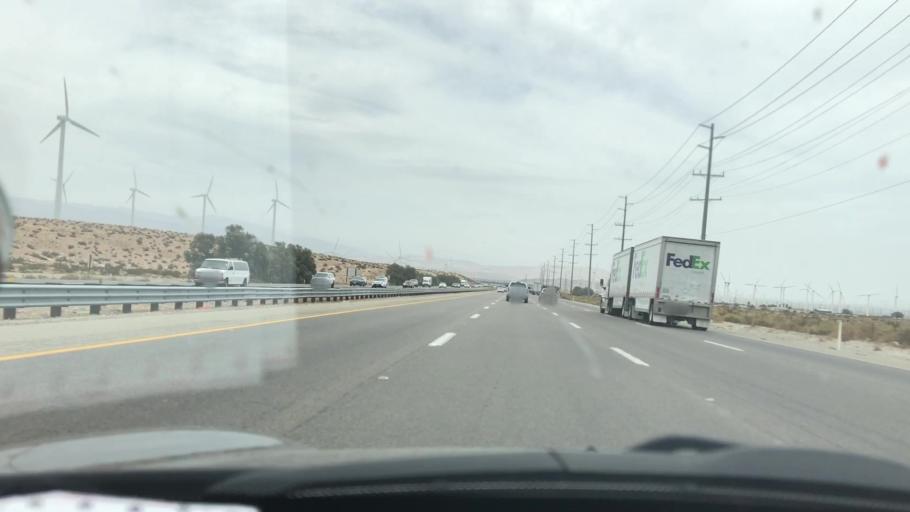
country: US
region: California
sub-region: Riverside County
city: Garnet
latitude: 33.9129
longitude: -116.5971
